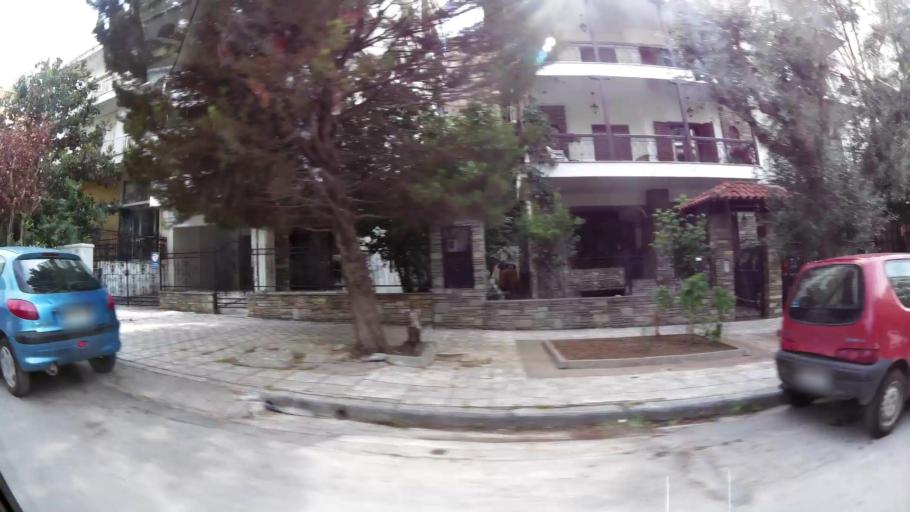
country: GR
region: Central Macedonia
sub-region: Nomos Thessalonikis
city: Kalamaria
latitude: 40.5878
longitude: 22.9513
